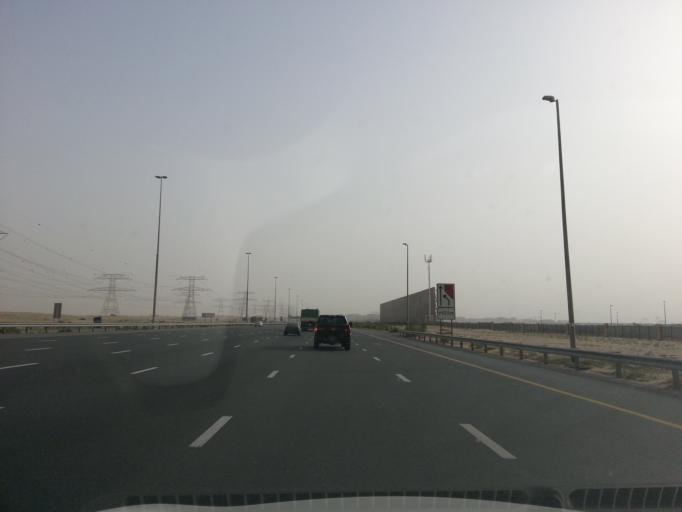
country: AE
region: Dubai
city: Dubai
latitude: 25.0190
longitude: 55.2774
